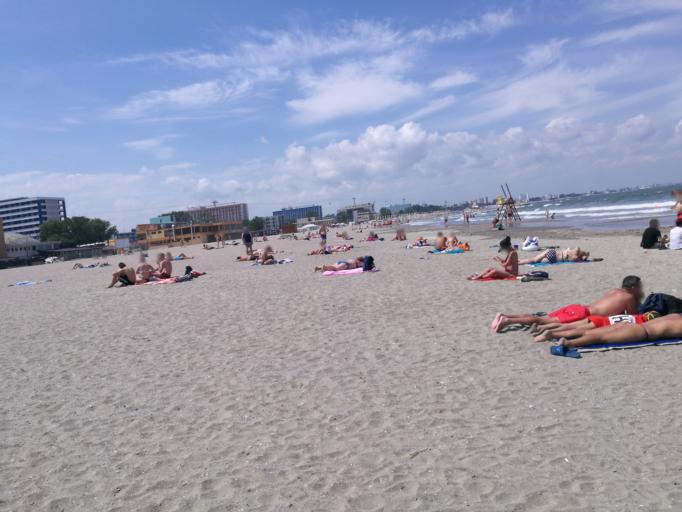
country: RO
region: Constanta
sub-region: Municipiul Constanta
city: Palazu Mare
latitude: 44.2225
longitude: 28.6354
